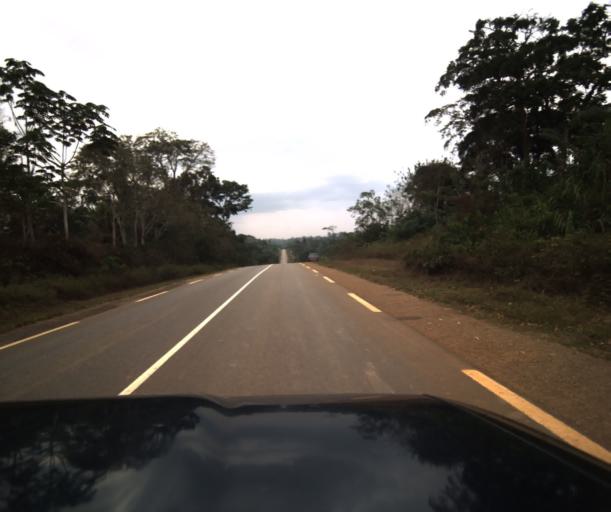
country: CM
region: Centre
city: Akono
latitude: 3.6313
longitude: 11.3240
